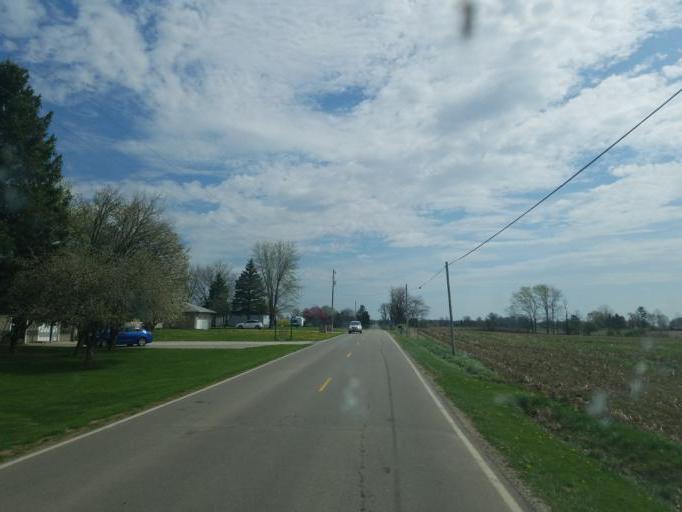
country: US
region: Ohio
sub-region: Crawford County
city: Bucyrus
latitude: 40.7891
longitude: -83.0131
